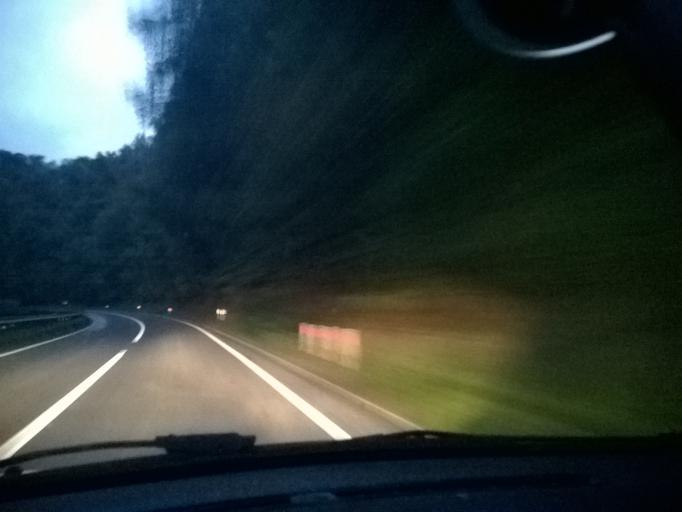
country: SI
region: Rogatec
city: Rogatec
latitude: 46.2217
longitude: 15.7295
